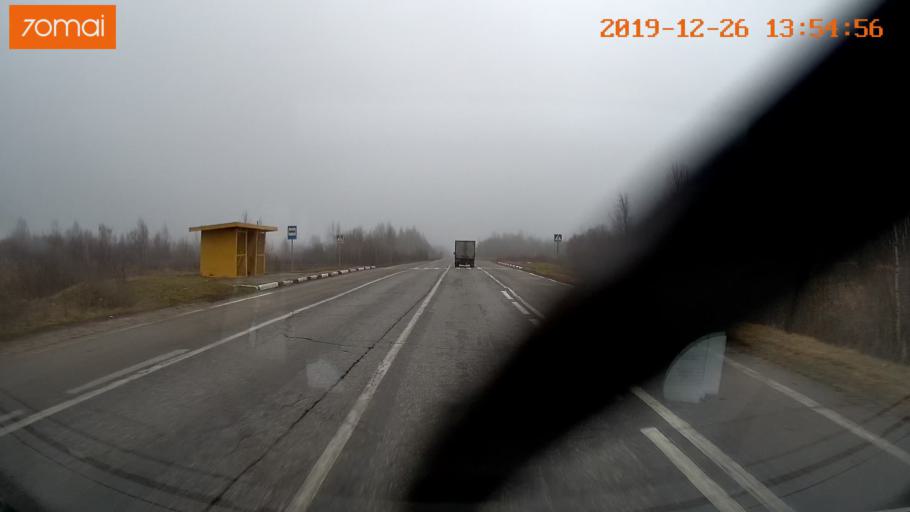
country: RU
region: Jaroslavl
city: Poshekhon'ye
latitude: 58.6086
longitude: 38.6414
